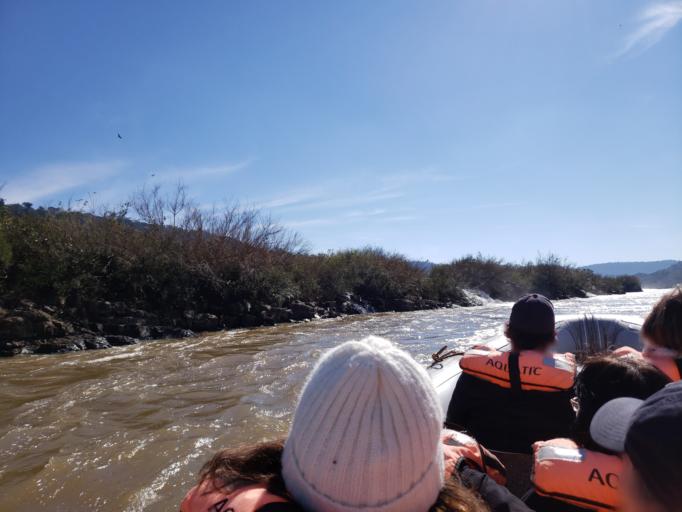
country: BR
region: Rio Grande do Sul
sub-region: Tres Passos
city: Tres Passos
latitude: -27.1537
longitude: -53.8889
